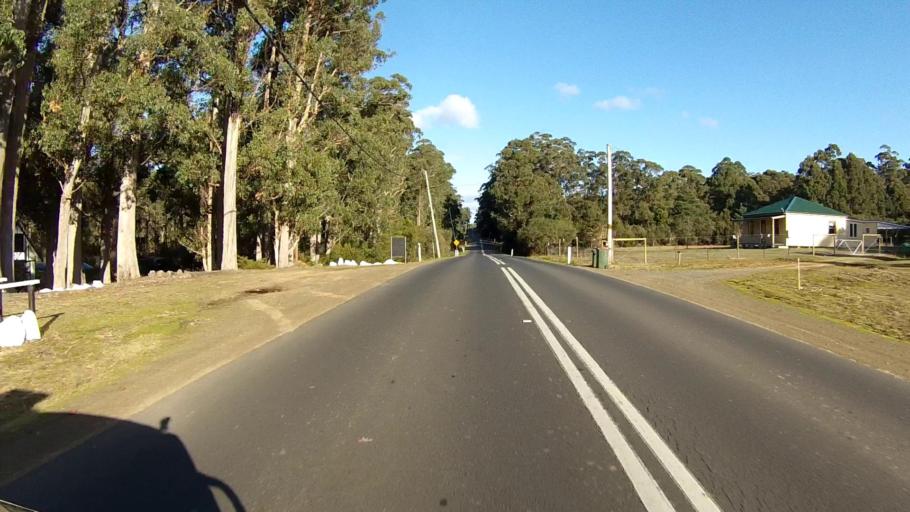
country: AU
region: Tasmania
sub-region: Clarence
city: Sandford
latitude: -43.1255
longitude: 147.8500
